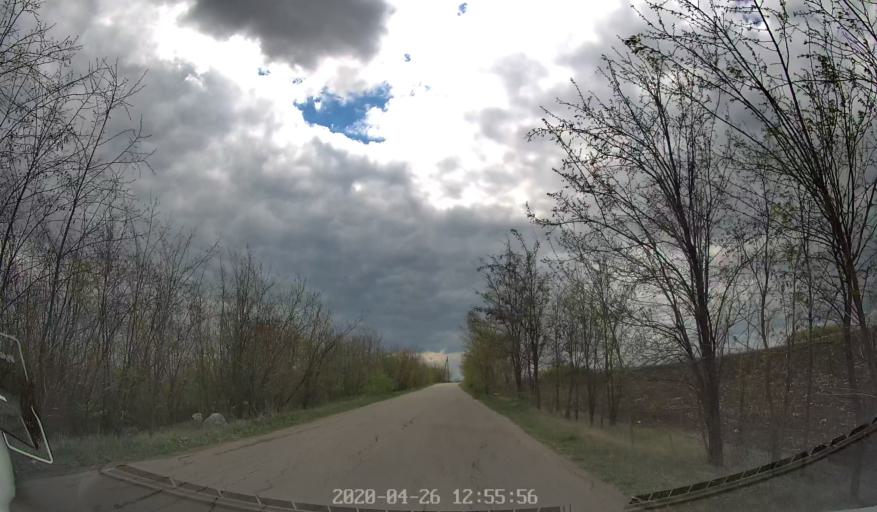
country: MD
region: Chisinau
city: Vadul lui Voda
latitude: 47.0756
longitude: 29.0661
